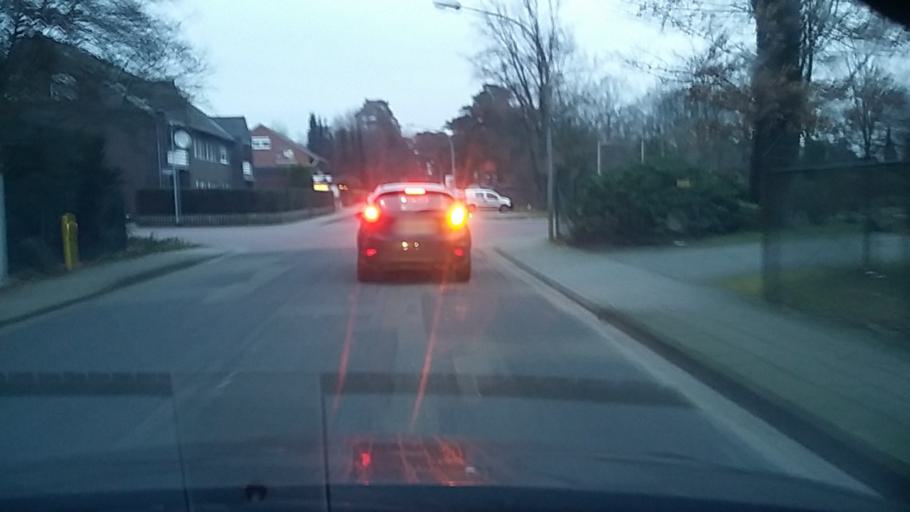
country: DE
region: Lower Saxony
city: Meppen
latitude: 52.6976
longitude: 7.2676
